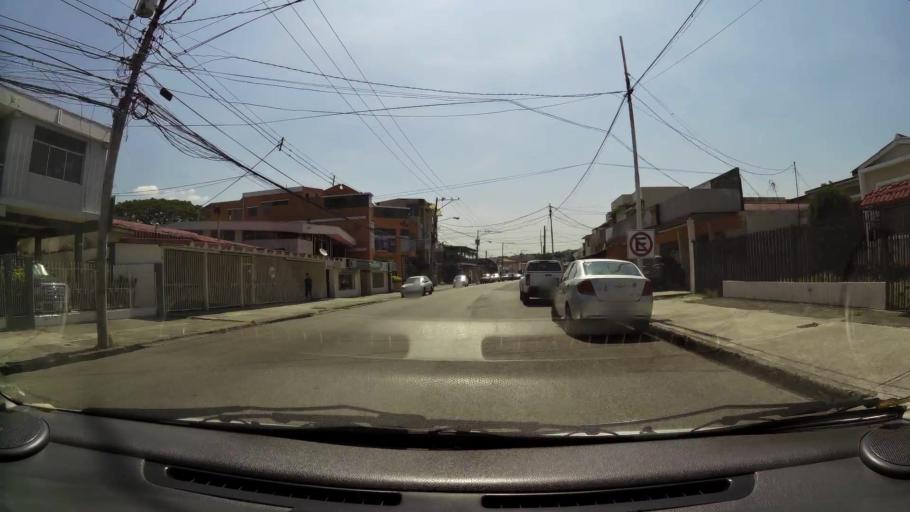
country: EC
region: Guayas
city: Guayaquil
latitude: -2.1703
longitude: -79.9116
